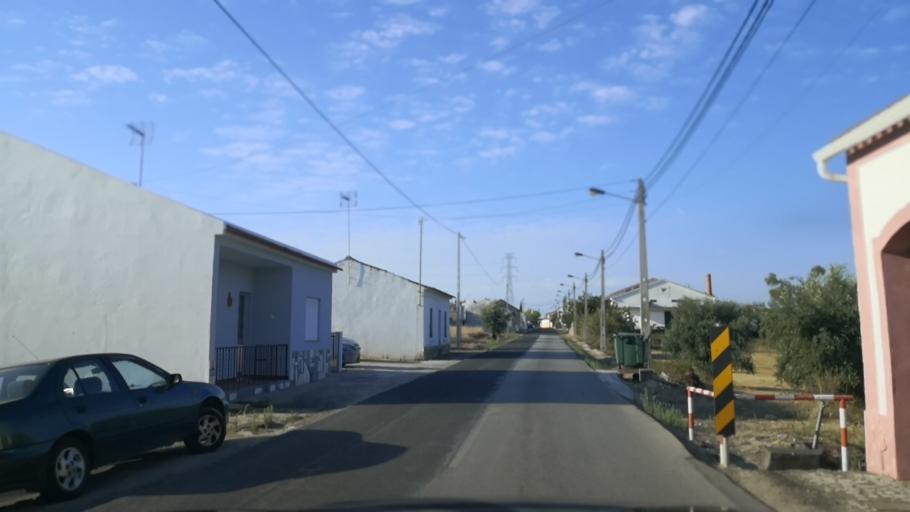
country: PT
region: Santarem
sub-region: Santarem
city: Santarem
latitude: 39.3013
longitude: -8.6609
